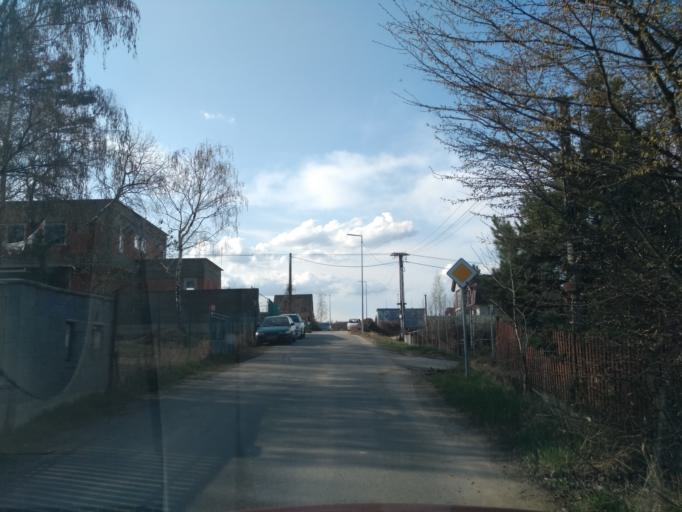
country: SK
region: Kosicky
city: Kosice
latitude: 48.6928
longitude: 21.2024
